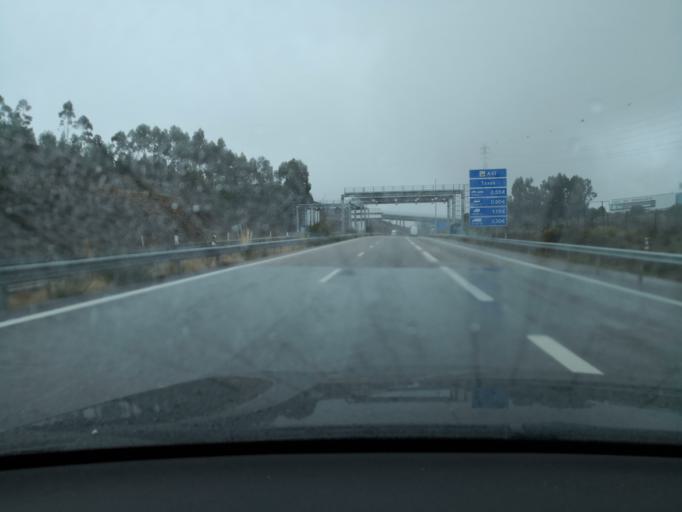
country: PT
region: Porto
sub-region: Pacos de Ferreira
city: Seroa
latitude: 41.2433
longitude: -8.4355
